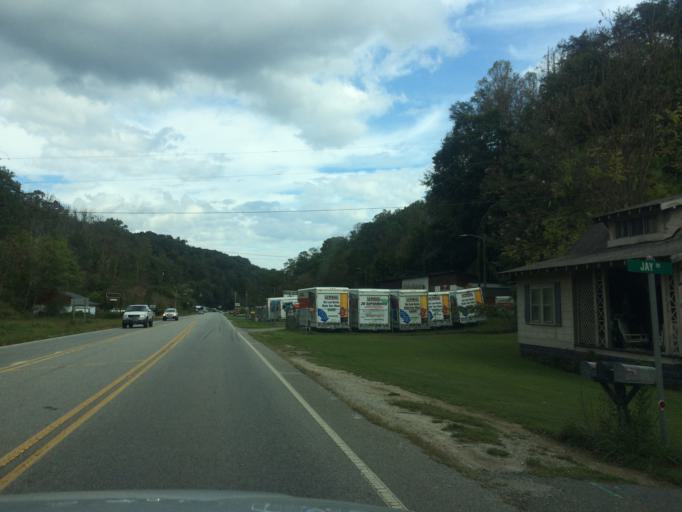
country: US
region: North Carolina
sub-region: Haywood County
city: Canton
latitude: 35.5347
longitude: -82.8199
